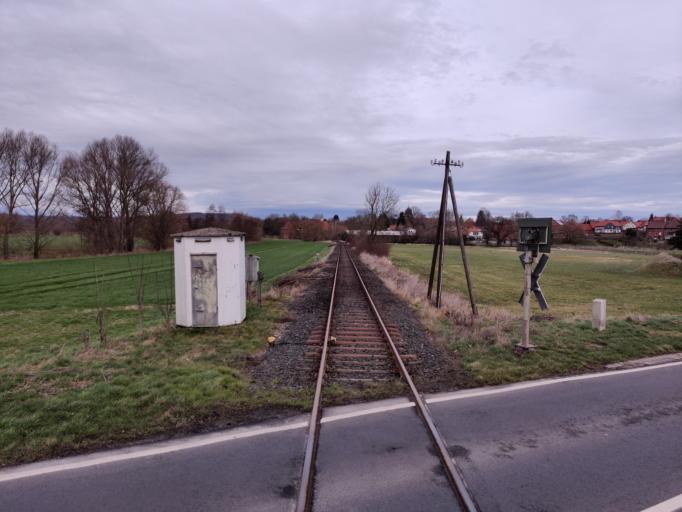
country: DE
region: Lower Saxony
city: Holle
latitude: 52.0838
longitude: 10.1543
